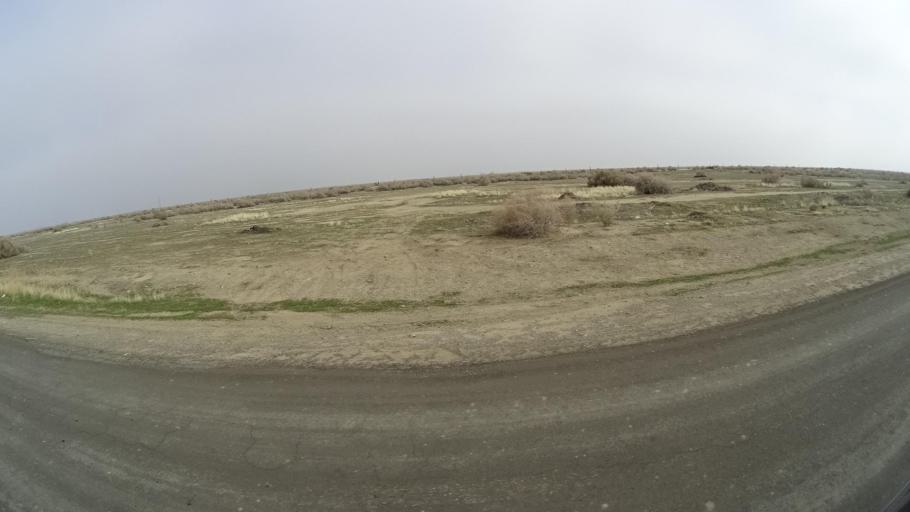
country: US
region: California
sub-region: Kern County
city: Maricopa
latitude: 35.0554
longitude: -119.3492
